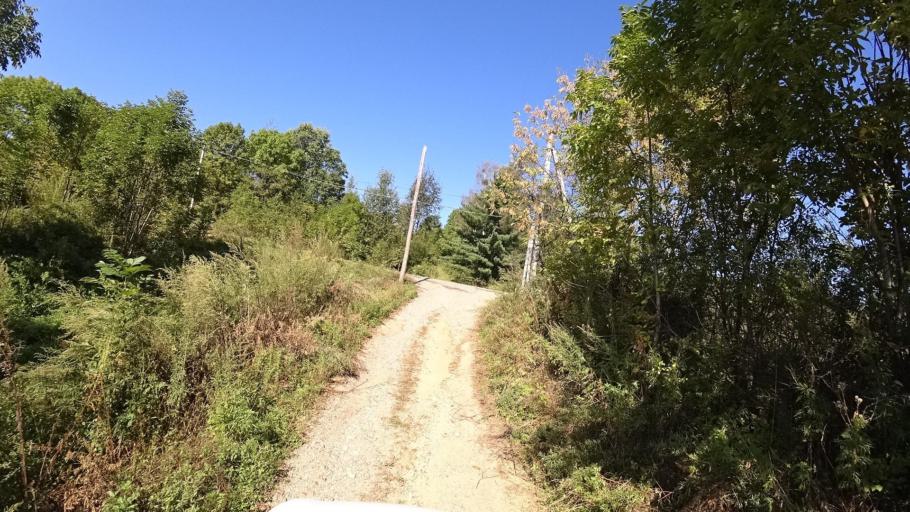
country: RU
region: Jewish Autonomous Oblast
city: Bira
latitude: 49.0097
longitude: 132.4735
